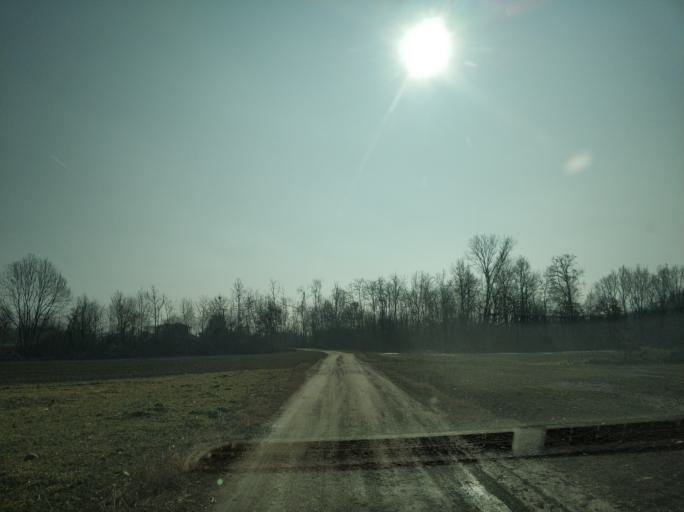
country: IT
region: Piedmont
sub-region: Provincia di Torino
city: Lombardore
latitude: 45.2427
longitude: 7.7388
